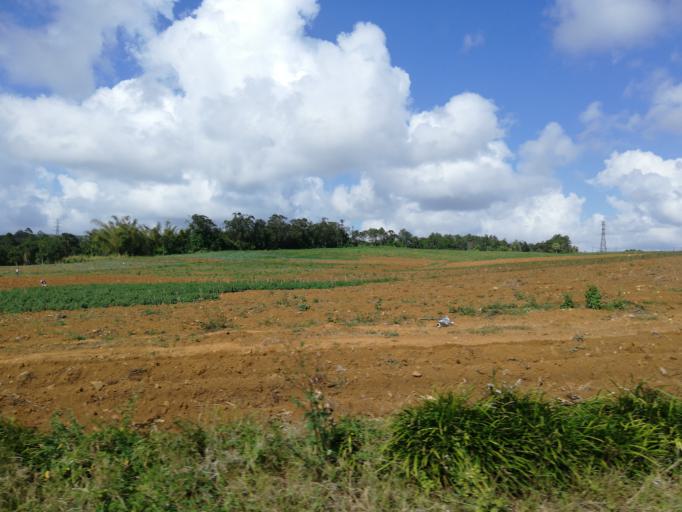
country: MU
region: Pamplemousses
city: Creve Coeur
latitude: -20.2074
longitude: 57.5581
